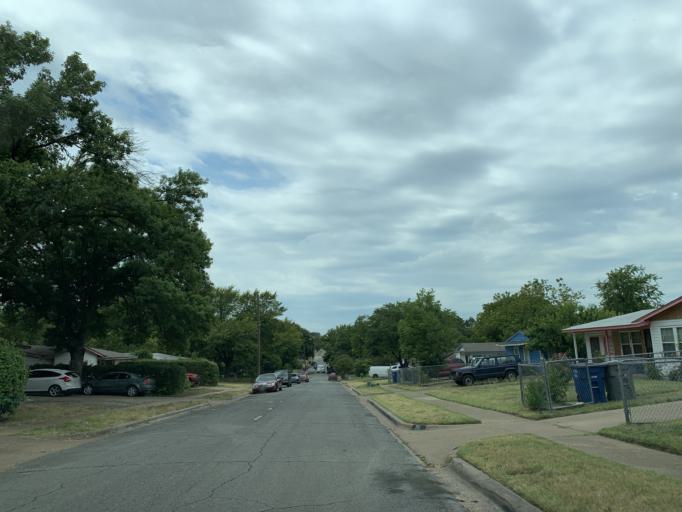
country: US
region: Texas
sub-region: Dallas County
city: DeSoto
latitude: 32.6608
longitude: -96.8322
